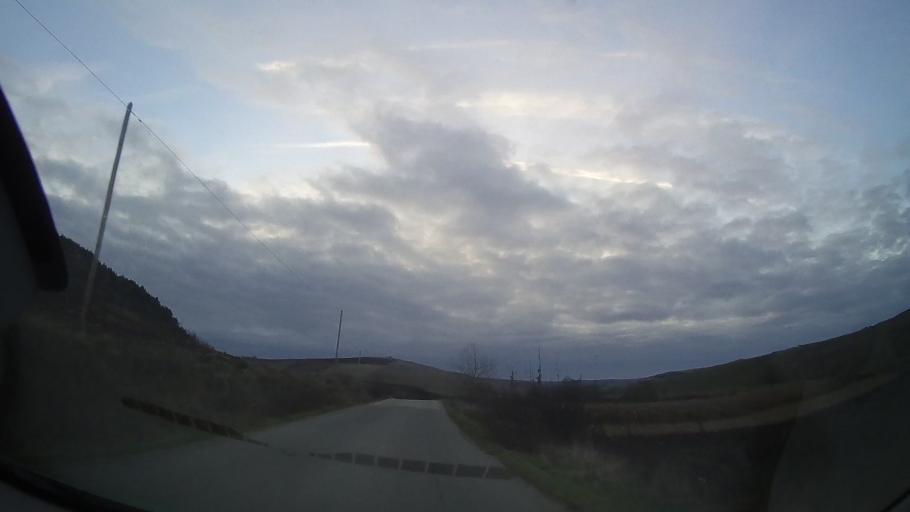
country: RO
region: Cluj
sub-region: Comuna Palatca
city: Palatca
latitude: 46.8650
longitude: 24.0051
